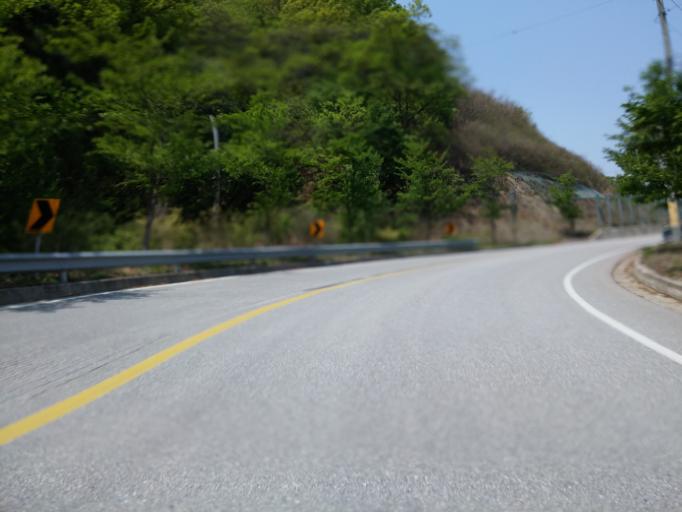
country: KR
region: Chungcheongbuk-do
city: Okcheon
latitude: 36.4322
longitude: 127.5813
